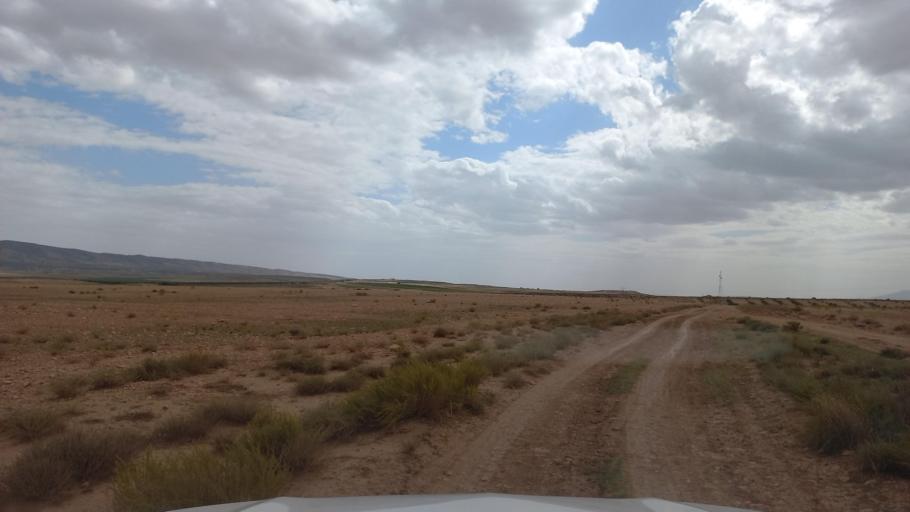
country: TN
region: Al Qasrayn
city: Sbiba
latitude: 35.3868
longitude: 9.1053
